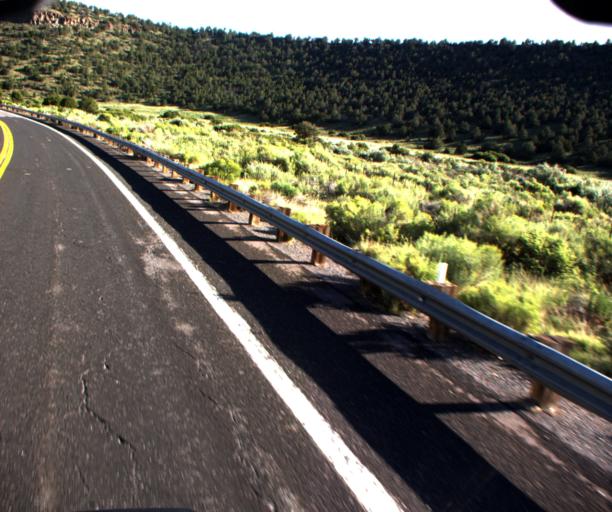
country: US
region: Arizona
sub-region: Apache County
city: Eagar
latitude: 34.0788
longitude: -109.1982
